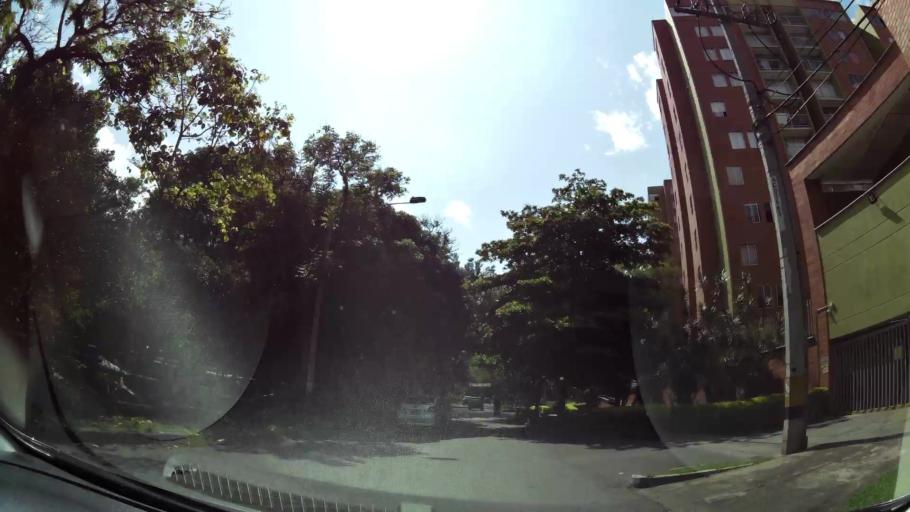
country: CO
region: Antioquia
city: Itagui
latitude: 6.2170
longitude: -75.5957
